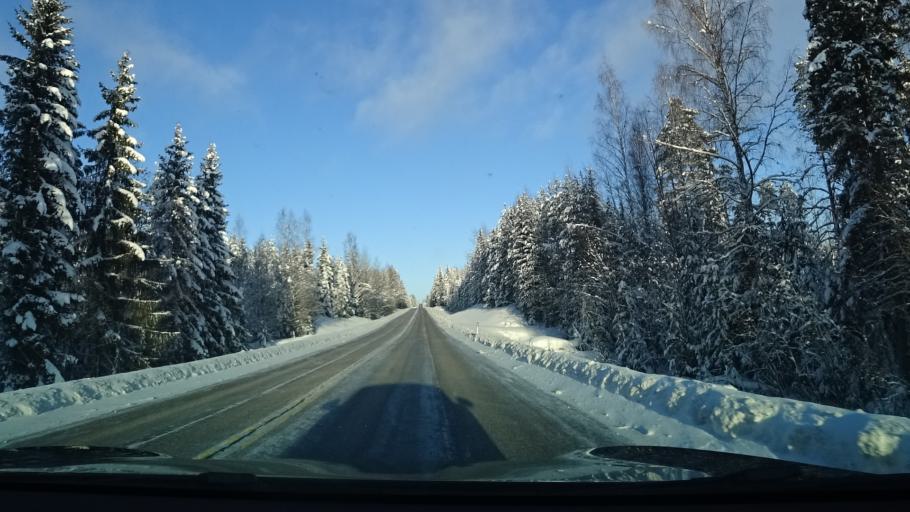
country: FI
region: Northern Savo
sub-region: Varkaus
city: Kangaslampi
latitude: 62.3836
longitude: 28.1316
